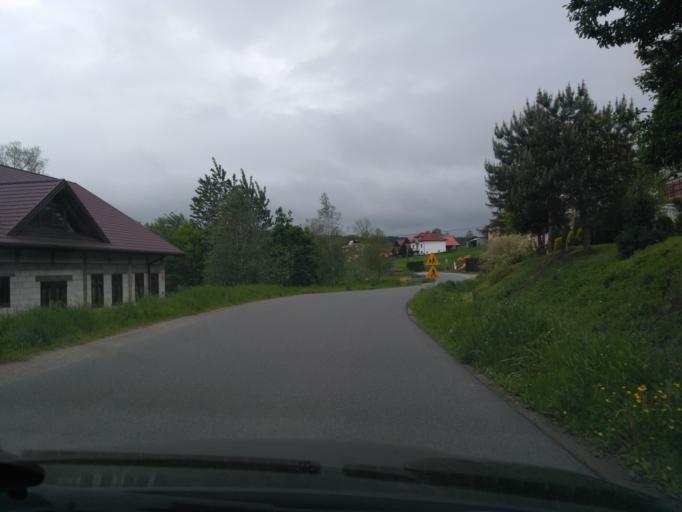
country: PL
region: Subcarpathian Voivodeship
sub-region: Powiat jasielski
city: Brzyska
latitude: 49.8535
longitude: 21.3425
